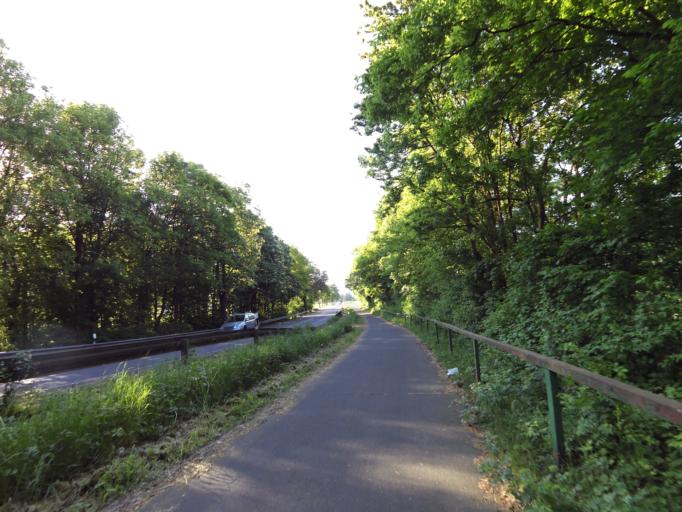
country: DE
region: North Rhine-Westphalia
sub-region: Regierungsbezirk Koln
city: Bonn
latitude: 50.6911
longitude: 7.0715
